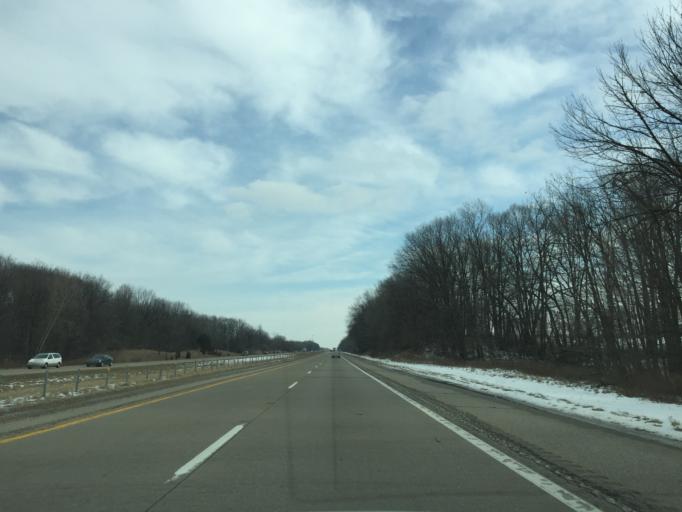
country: US
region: Michigan
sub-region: Ionia County
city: Saranac
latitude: 42.8792
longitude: -85.2035
